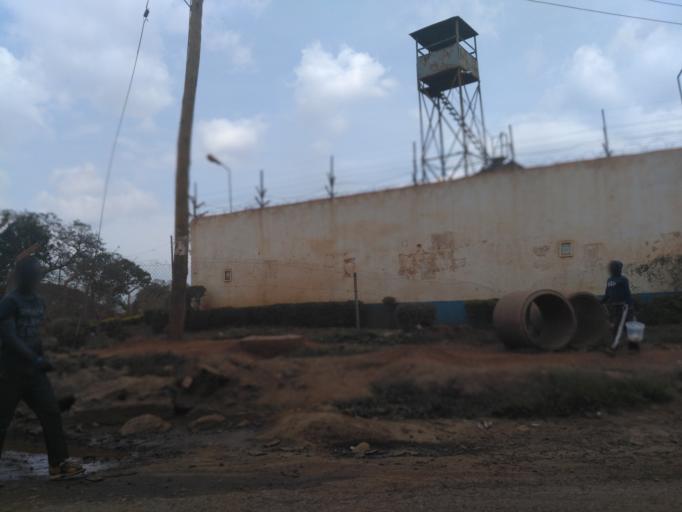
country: UG
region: Eastern Region
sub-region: Jinja District
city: Jinja
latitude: 0.4370
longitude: 33.2124
